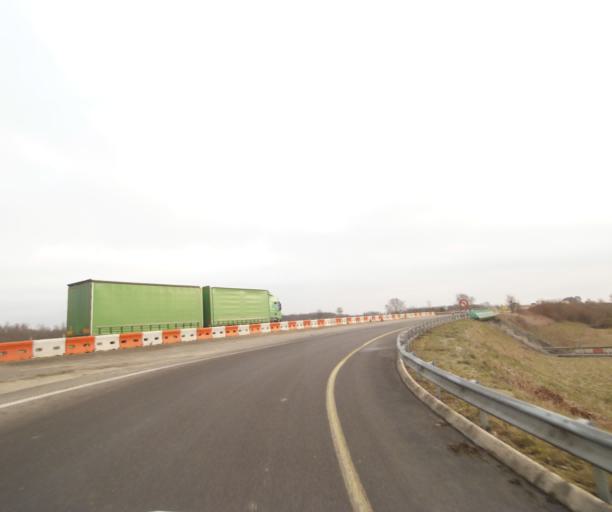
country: FR
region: Champagne-Ardenne
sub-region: Departement de la Haute-Marne
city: Villiers-en-Lieu
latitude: 48.6404
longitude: 4.9128
